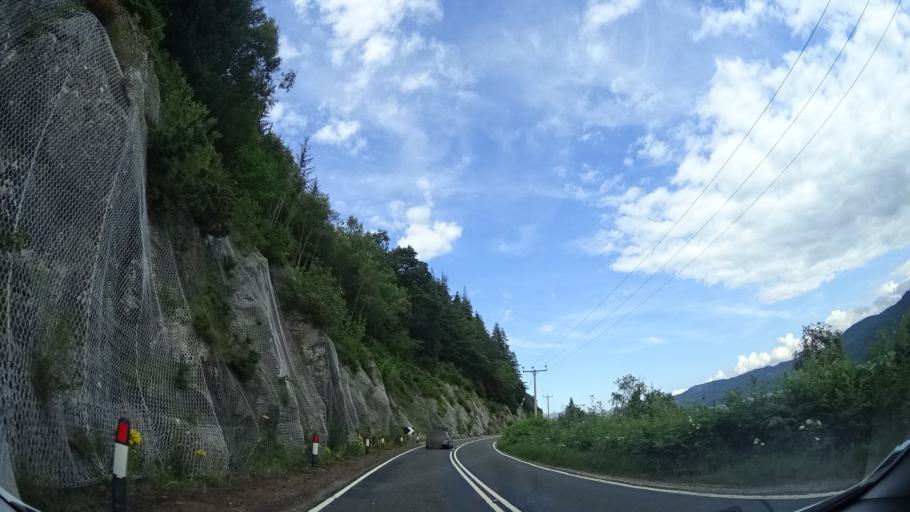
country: GB
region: Scotland
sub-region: Highland
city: Beauly
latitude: 57.2446
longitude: -4.5441
